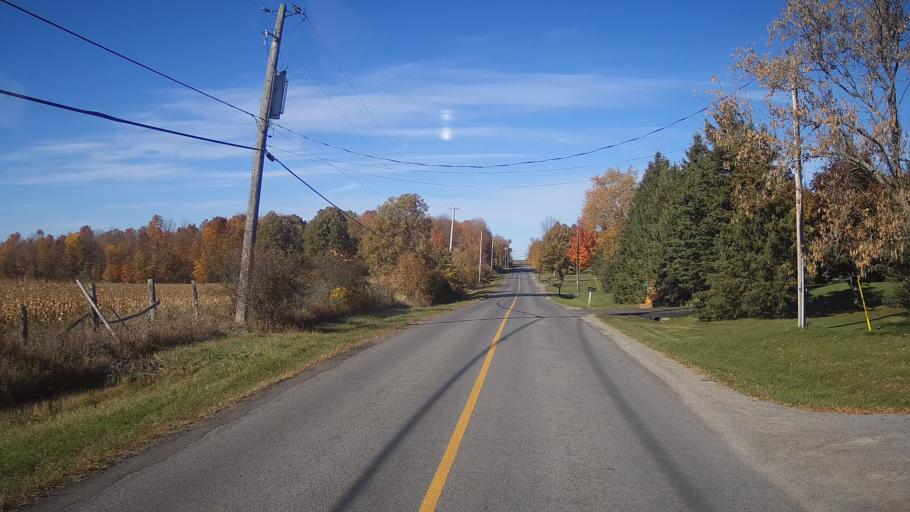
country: CA
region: Ontario
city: Kingston
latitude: 44.4110
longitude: -76.5275
